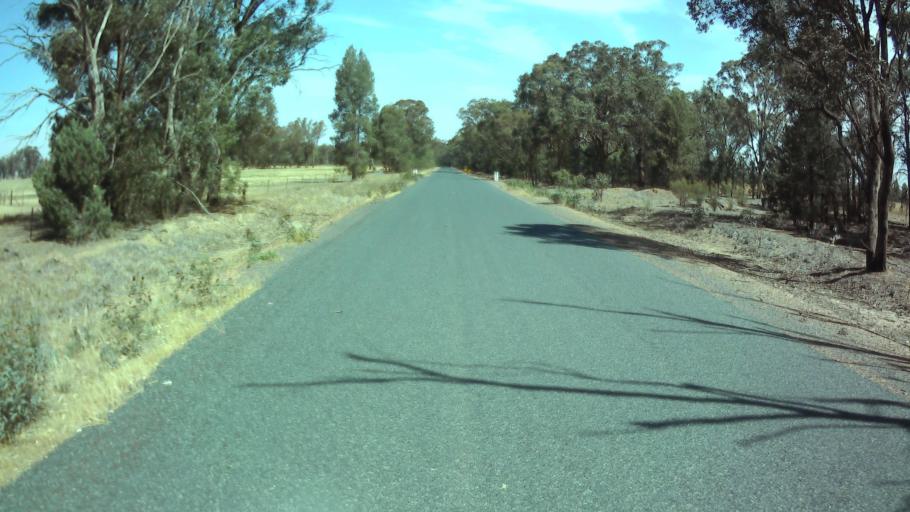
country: AU
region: New South Wales
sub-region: Weddin
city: Grenfell
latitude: -34.0660
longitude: 148.1365
